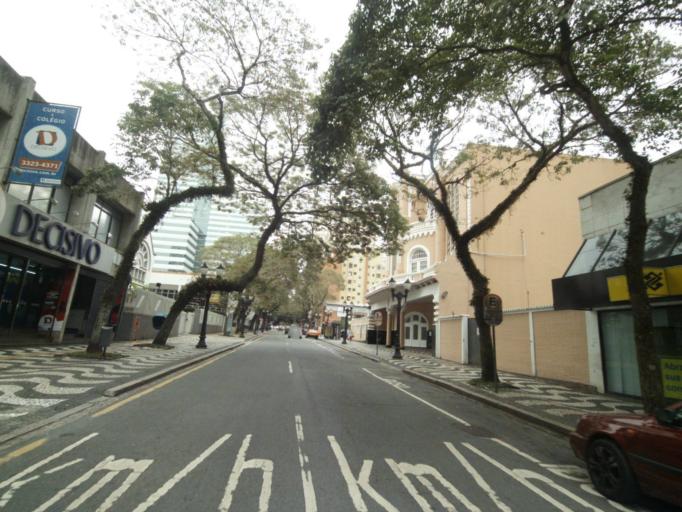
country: BR
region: Parana
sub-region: Curitiba
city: Curitiba
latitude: -25.4356
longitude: -49.2787
